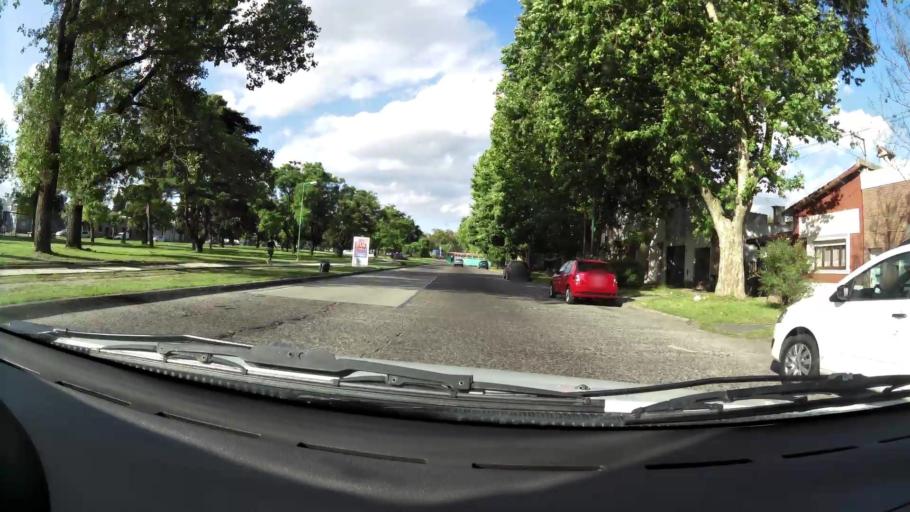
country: AR
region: Buenos Aires
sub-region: Partido de La Plata
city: La Plata
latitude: -34.8966
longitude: -57.9645
